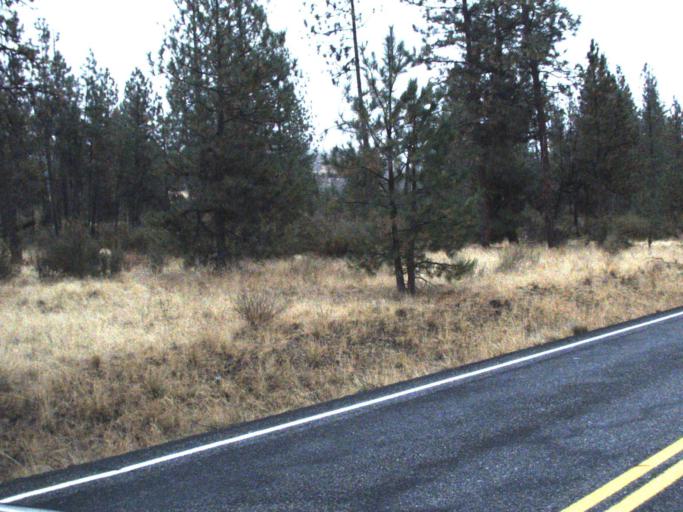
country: US
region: Washington
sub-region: Lincoln County
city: Davenport
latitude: 47.7938
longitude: -117.8908
